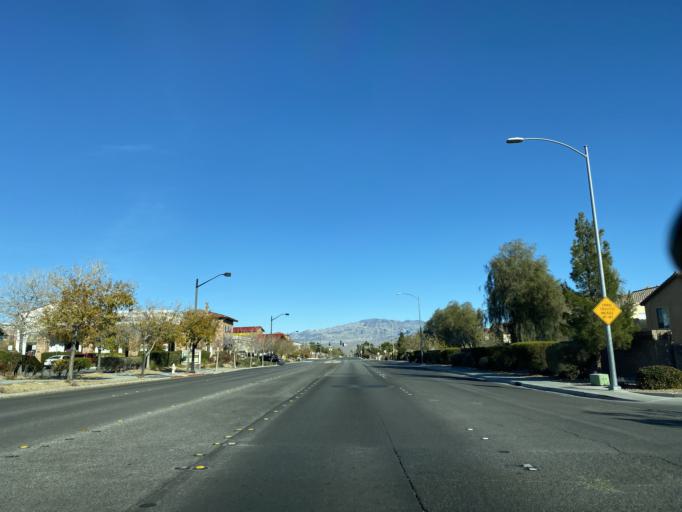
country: US
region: Nevada
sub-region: Clark County
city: Las Vegas
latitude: 36.2970
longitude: -115.2786
